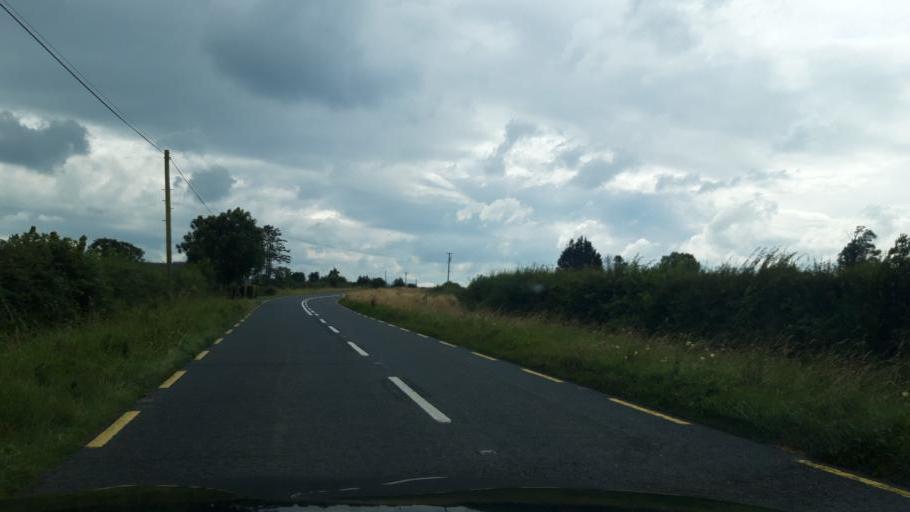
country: IE
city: Ballylinan
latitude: 52.9180
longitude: -7.0674
